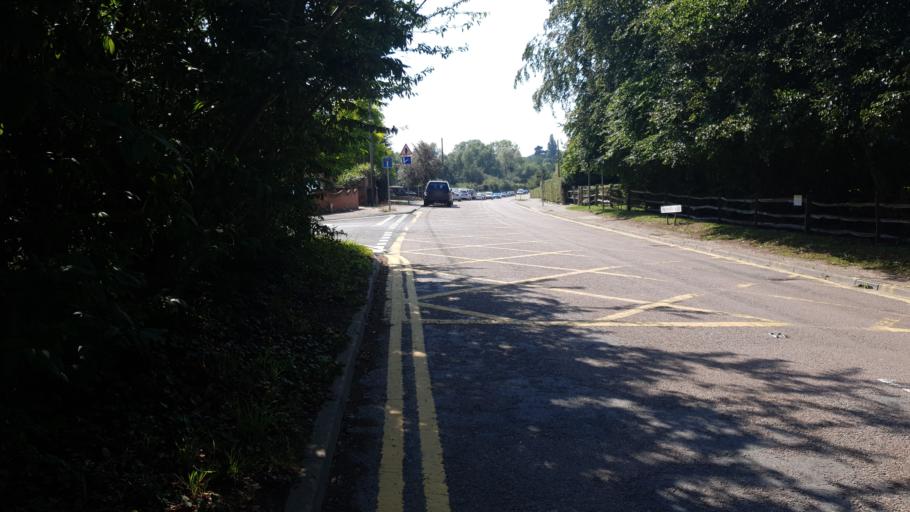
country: GB
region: England
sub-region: Essex
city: Colchester
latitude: 51.9247
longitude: 0.9393
